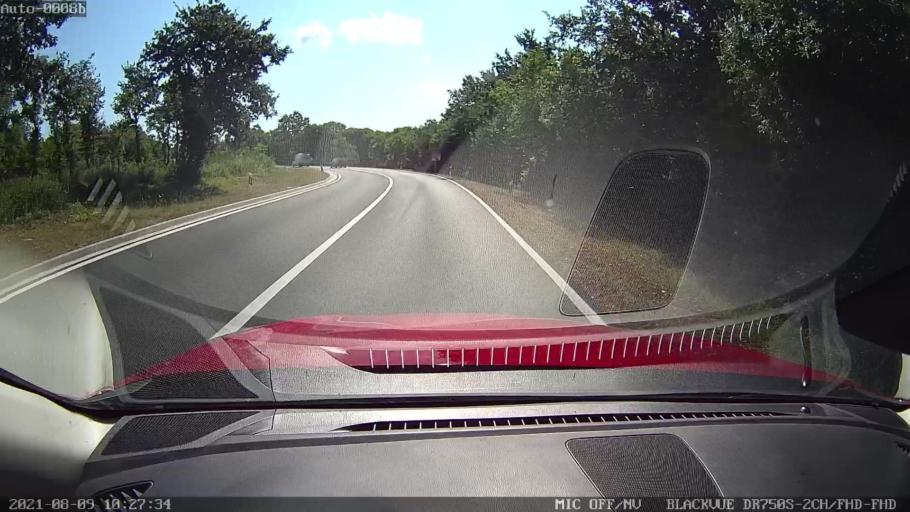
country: HR
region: Istarska
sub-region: Grad Rovinj
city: Rovinj
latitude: 45.1096
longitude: 13.7945
